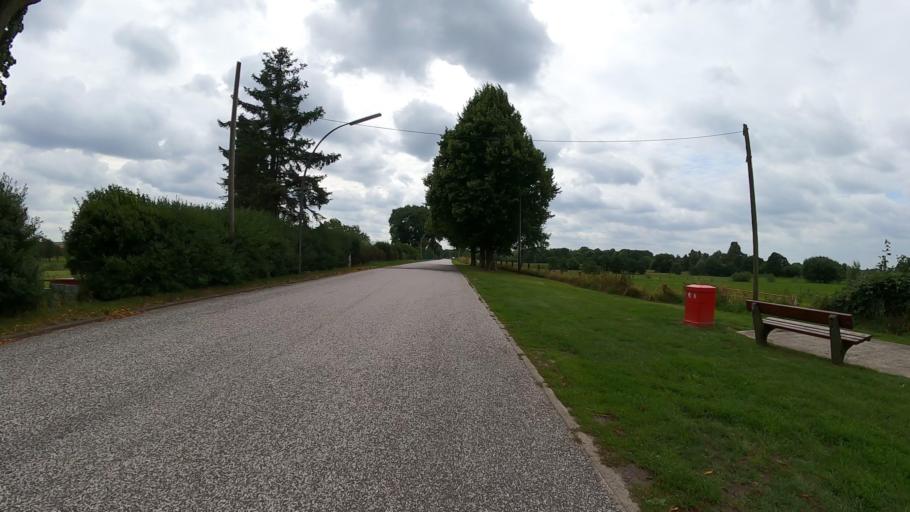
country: DE
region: Lower Saxony
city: Neu Wulmstorf
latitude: 53.5244
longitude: 9.8445
